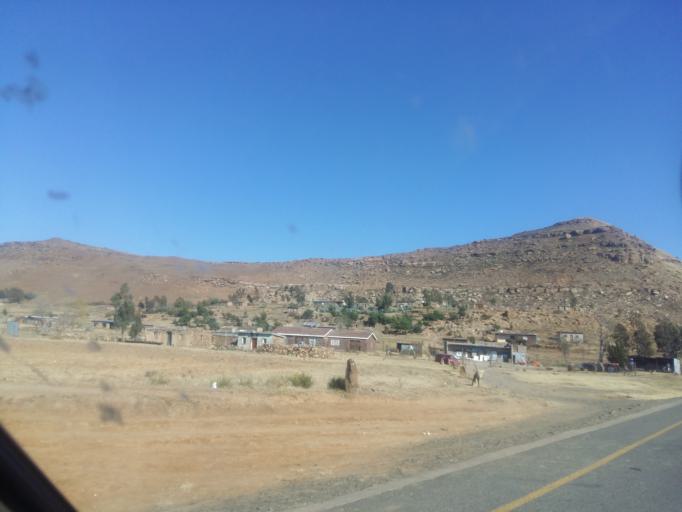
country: LS
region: Mafeteng
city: Mafeteng
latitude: -29.6940
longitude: 27.2826
